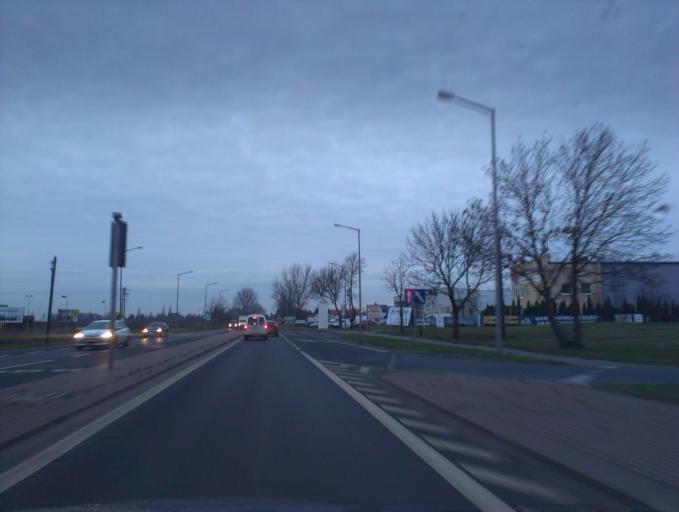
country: PL
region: Greater Poland Voivodeship
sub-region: Powiat poznanski
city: Zlotniki
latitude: 52.4864
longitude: 16.8540
